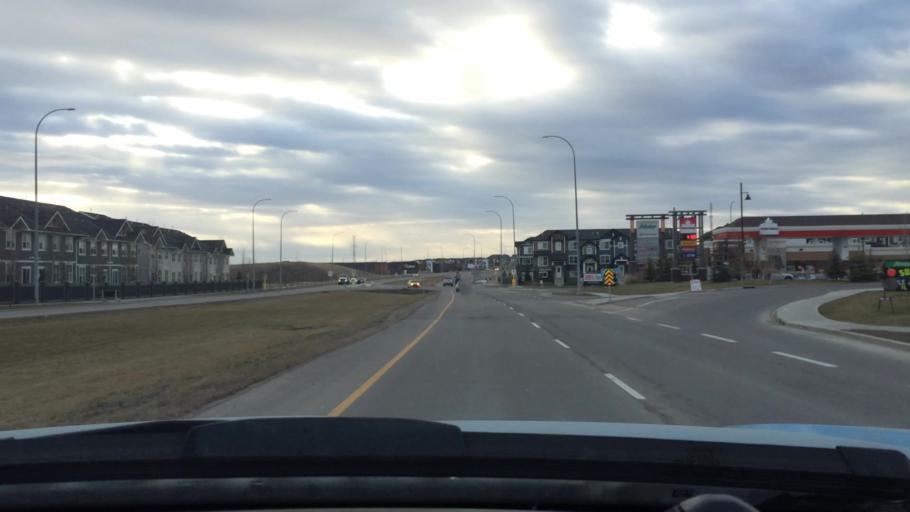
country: CA
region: Alberta
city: Calgary
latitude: 51.1740
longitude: -114.1560
